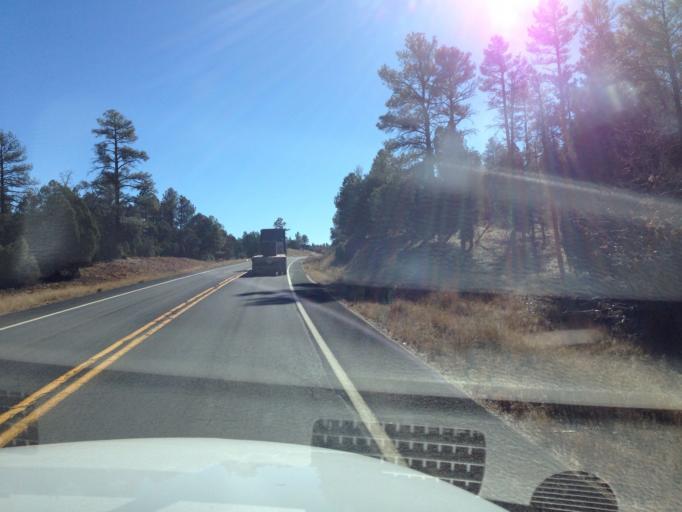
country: US
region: Arizona
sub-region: Navajo County
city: Linden
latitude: 34.2793
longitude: -110.0979
